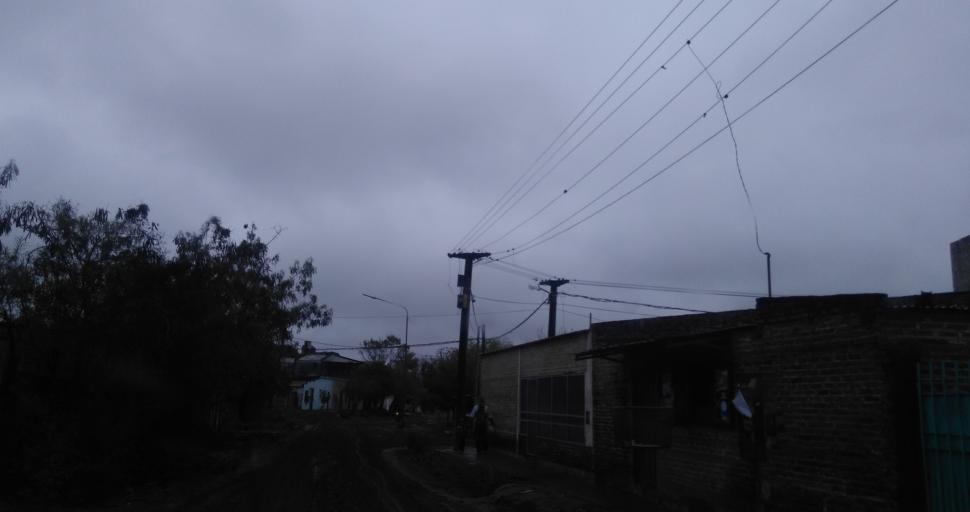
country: AR
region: Chaco
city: Fontana
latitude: -27.4259
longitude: -59.0243
